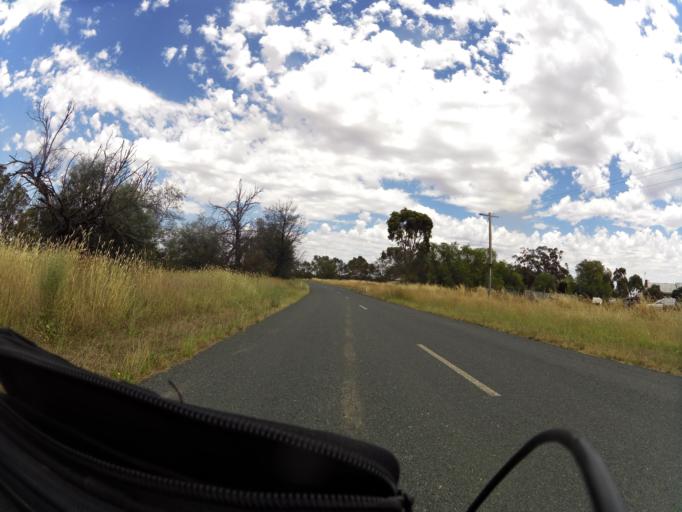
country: AU
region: Victoria
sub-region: Greater Shepparton
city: Shepparton
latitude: -36.6689
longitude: 145.1973
